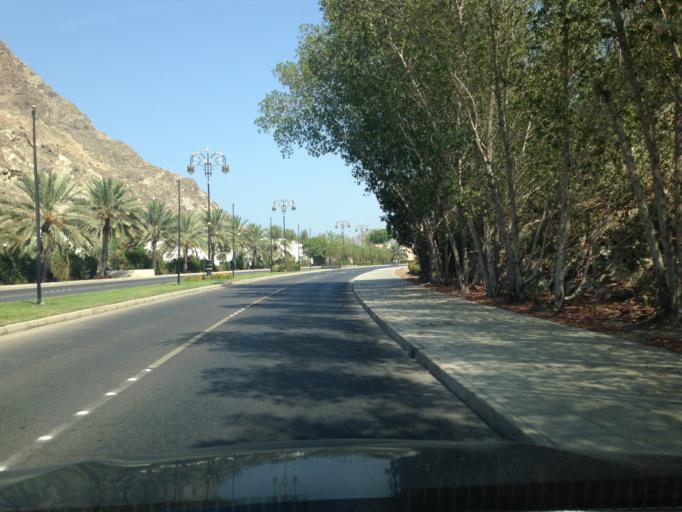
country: OM
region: Muhafazat Masqat
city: Muscat
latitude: 23.6205
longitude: 58.5841
